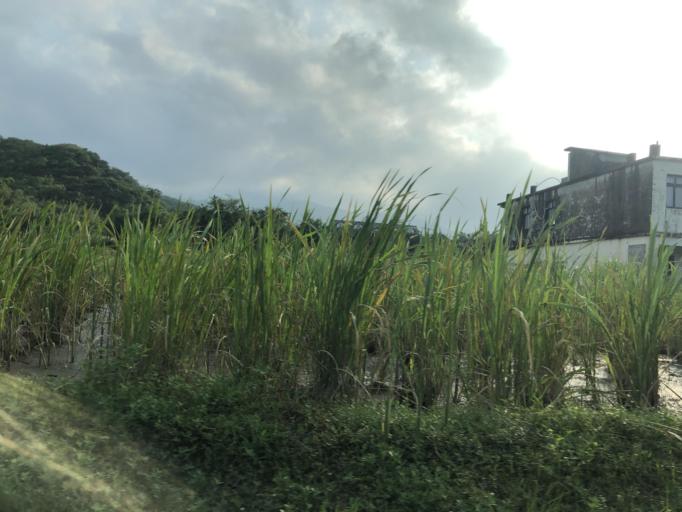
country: TW
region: Taiwan
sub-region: Keelung
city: Keelung
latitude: 25.2111
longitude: 121.6463
